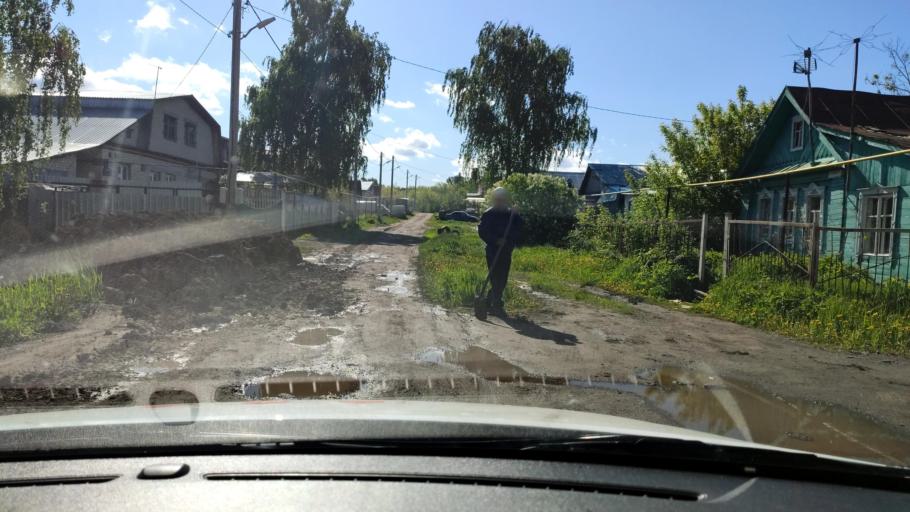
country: RU
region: Tatarstan
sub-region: Gorod Kazan'
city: Kazan
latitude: 55.7357
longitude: 49.0901
